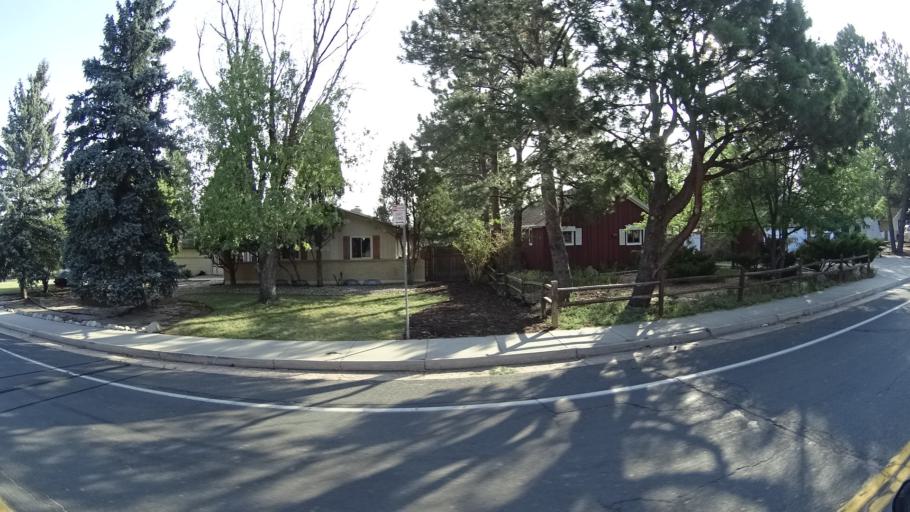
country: US
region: Colorado
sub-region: El Paso County
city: Colorado Springs
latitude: 38.8144
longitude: -104.8596
